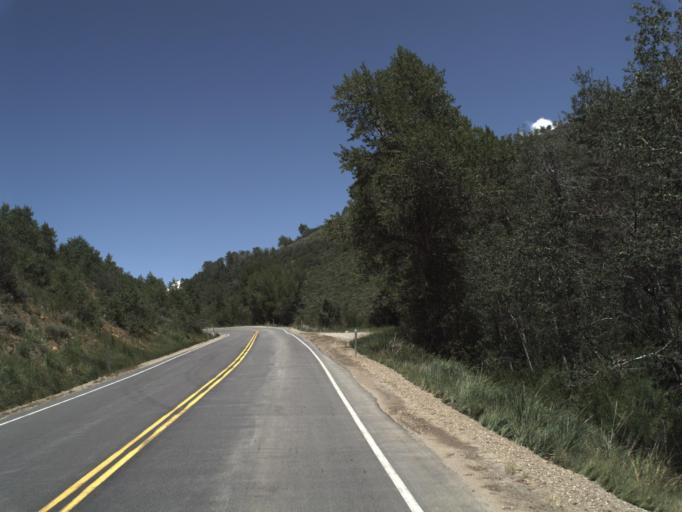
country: US
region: Utah
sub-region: Weber County
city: Wolf Creek
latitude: 41.3987
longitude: -111.5997
